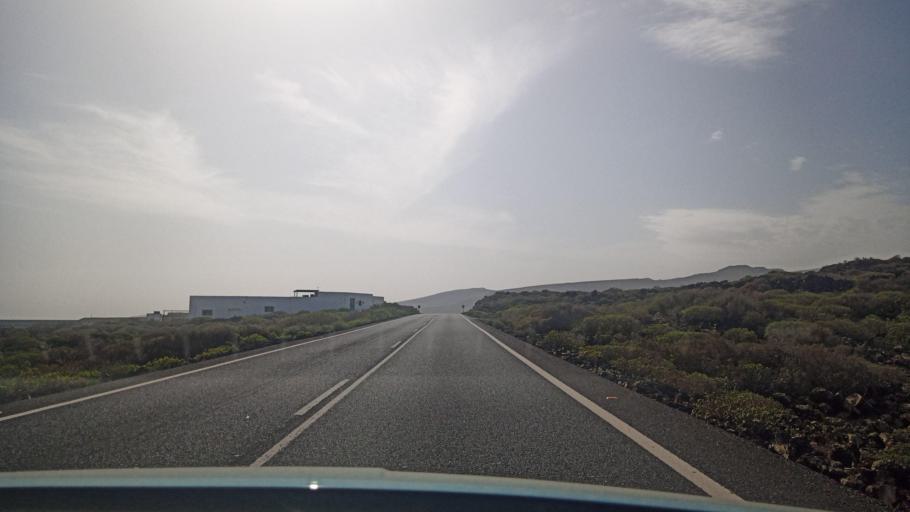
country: ES
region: Canary Islands
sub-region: Provincia de Las Palmas
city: Haria
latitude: 29.1445
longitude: -13.4526
